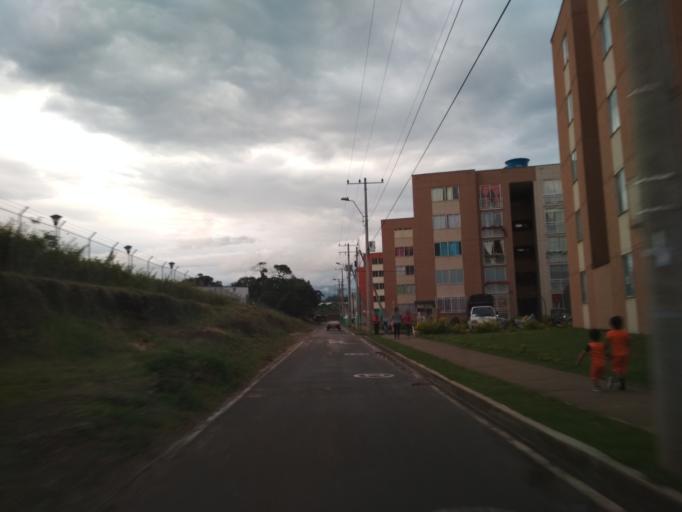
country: CO
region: Cauca
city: Popayan
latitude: 2.4569
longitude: -76.6409
